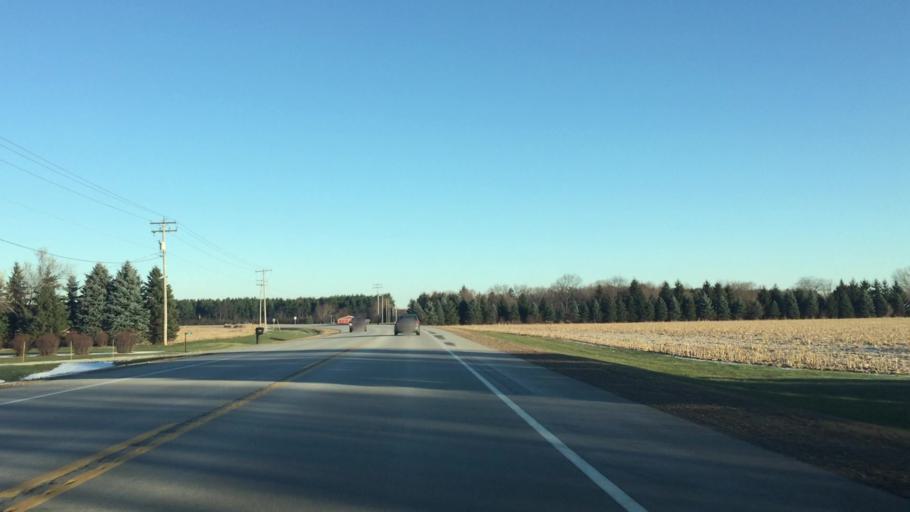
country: US
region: Wisconsin
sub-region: Waukesha County
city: Dousman
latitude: 43.0380
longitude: -88.4622
